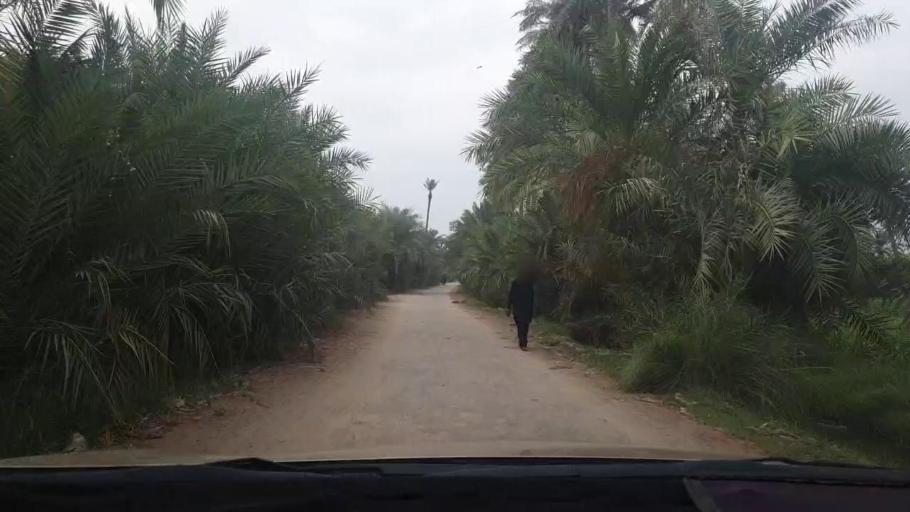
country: PK
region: Sindh
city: Larkana
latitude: 27.5642
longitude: 68.2303
